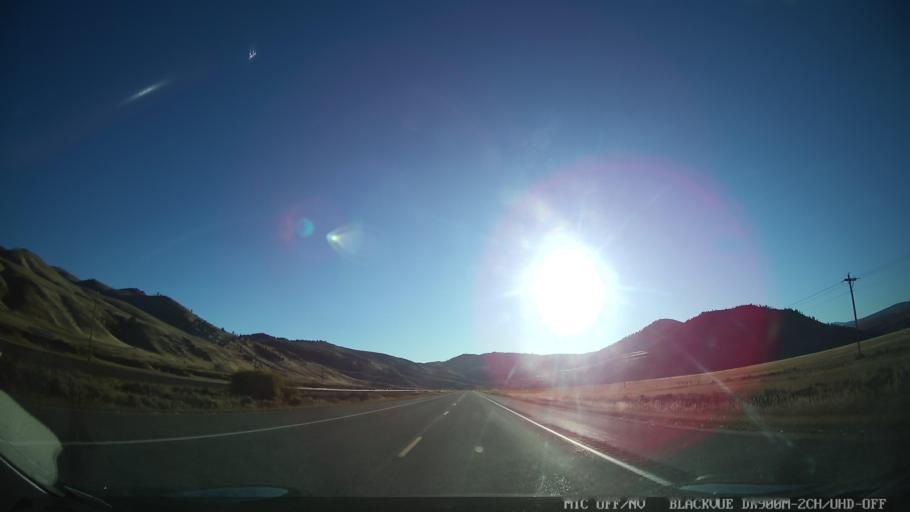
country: US
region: Colorado
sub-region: Grand County
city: Hot Sulphur Springs
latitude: 40.0520
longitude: -106.1513
